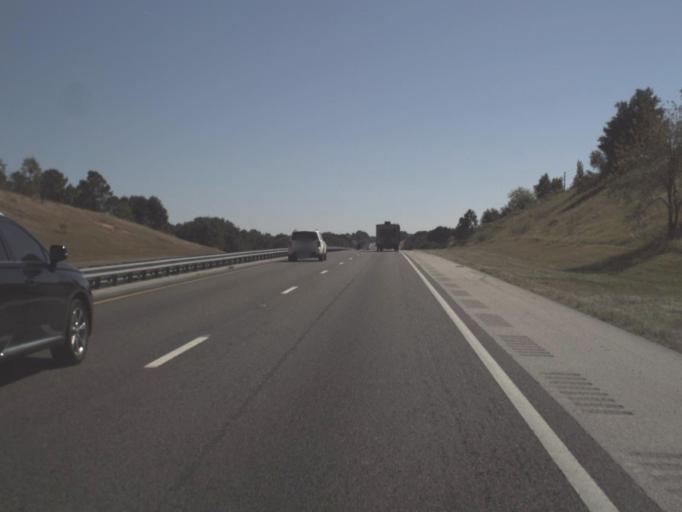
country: US
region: Florida
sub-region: Lake County
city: Montverde
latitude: 28.5715
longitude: -81.6956
